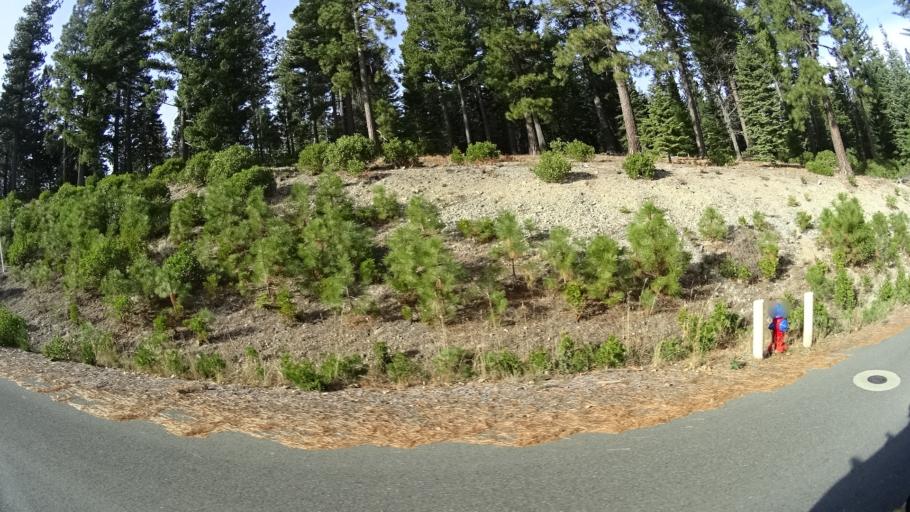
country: US
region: California
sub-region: Siskiyou County
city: Weed
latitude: 41.3969
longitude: -122.3916
